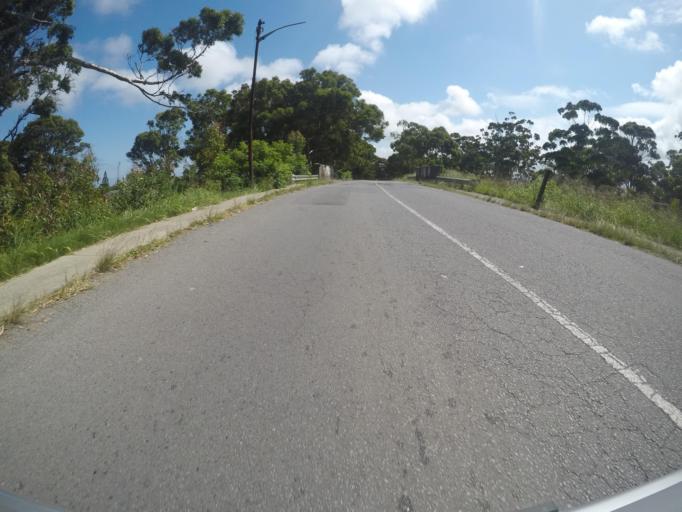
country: ZA
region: Eastern Cape
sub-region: Buffalo City Metropolitan Municipality
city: East London
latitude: -32.9996
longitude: 27.8914
